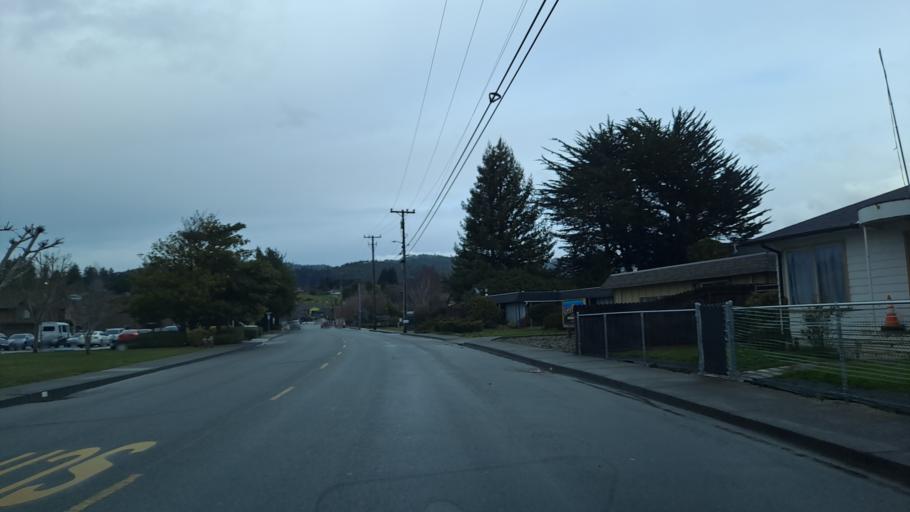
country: US
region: California
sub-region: Humboldt County
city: Fortuna
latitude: 40.5898
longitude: -124.1417
